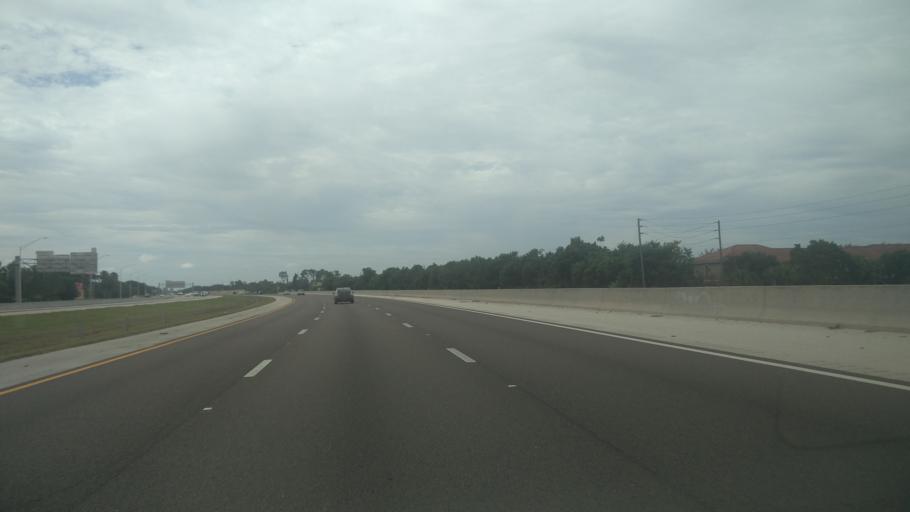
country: US
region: Florida
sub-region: Lee County
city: Three Oaks
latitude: 26.4869
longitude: -81.7945
